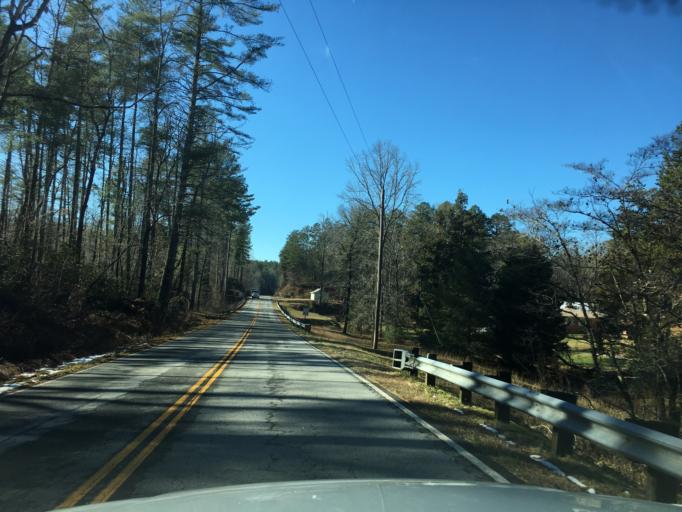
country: US
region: South Carolina
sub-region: Oconee County
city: Walhalla
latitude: 34.9357
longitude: -82.9959
